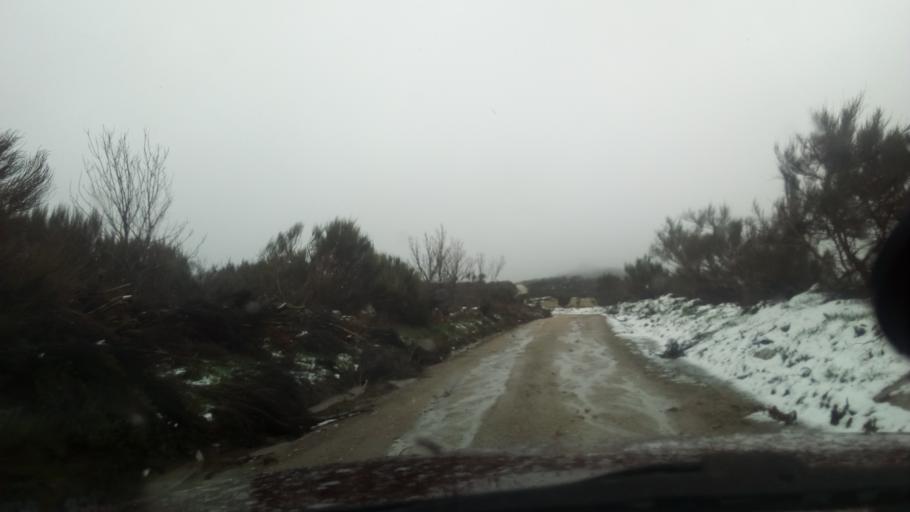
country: PT
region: Guarda
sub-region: Celorico da Beira
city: Celorico da Beira
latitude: 40.5276
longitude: -7.4467
